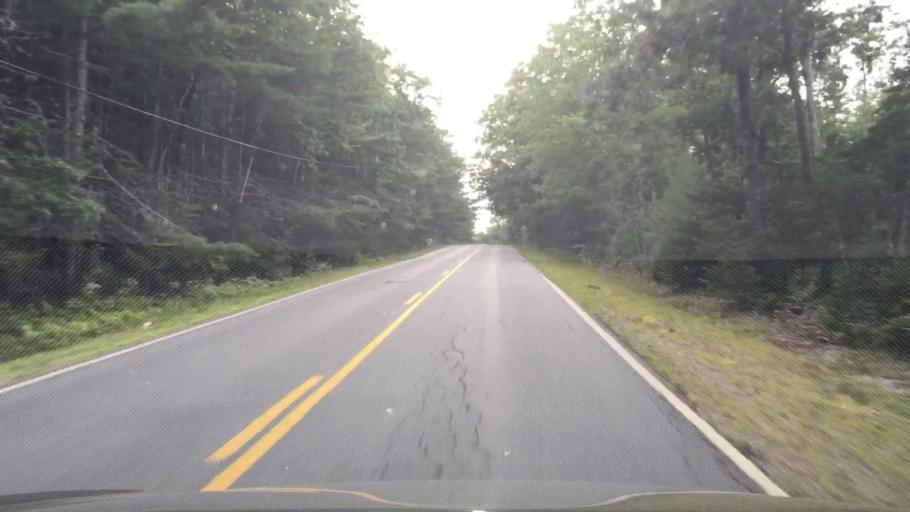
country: US
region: Maine
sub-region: Hancock County
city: Penobscot
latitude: 44.4513
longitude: -68.6866
